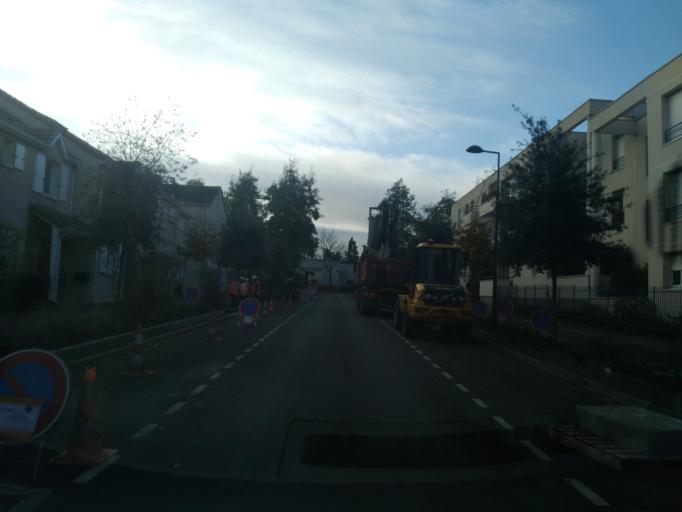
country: FR
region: Ile-de-France
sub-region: Departement des Yvelines
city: Plaisir
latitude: 48.8195
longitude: 1.9604
